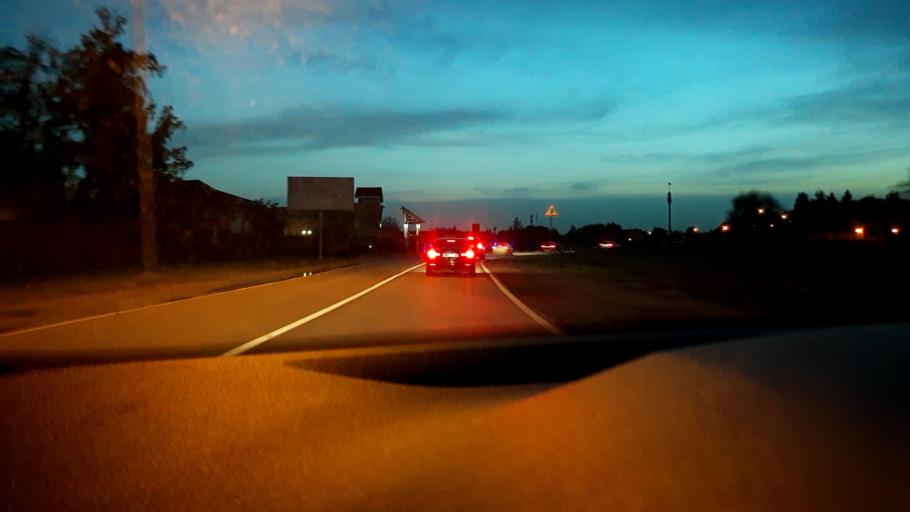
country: RU
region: Moskovskaya
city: Opalikha
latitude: 55.7865
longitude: 37.2270
